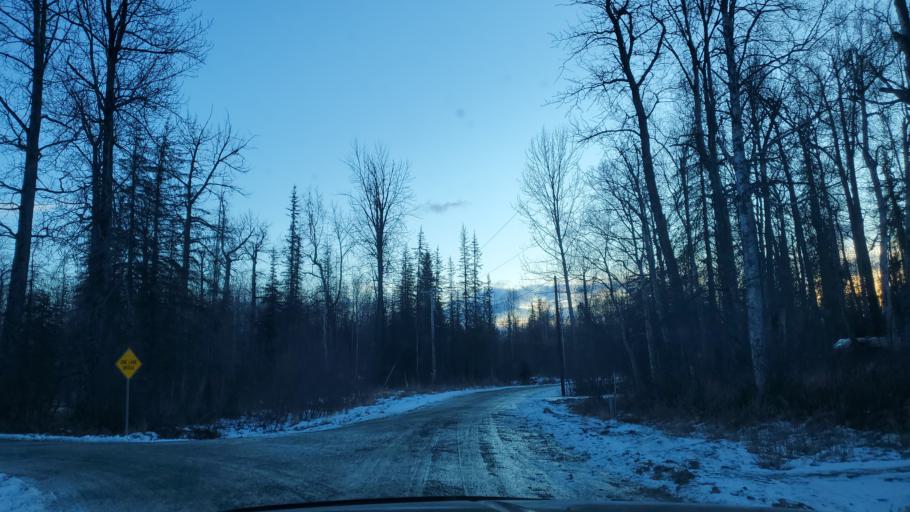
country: US
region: Alaska
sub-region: Matanuska-Susitna Borough
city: Lakes
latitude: 61.6660
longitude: -149.3408
